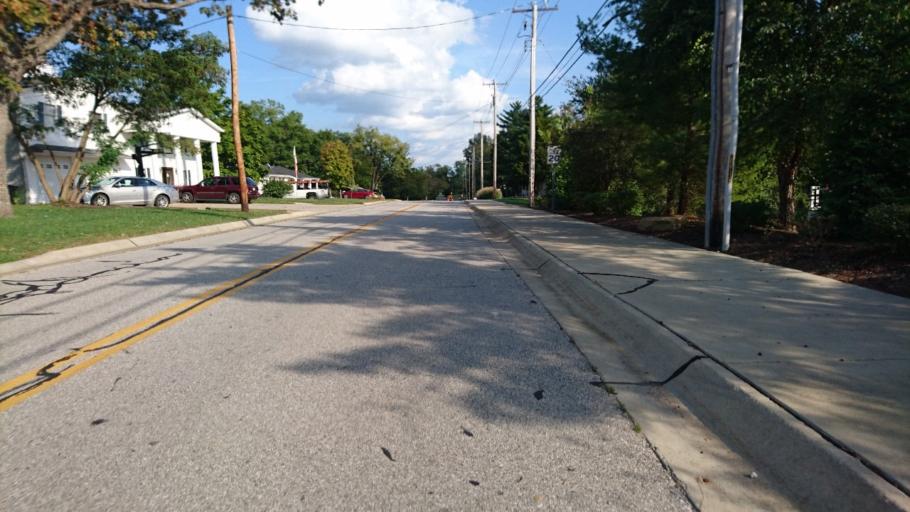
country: US
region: Missouri
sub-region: Saint Louis County
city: Eureka
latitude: 38.5114
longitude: -90.6306
